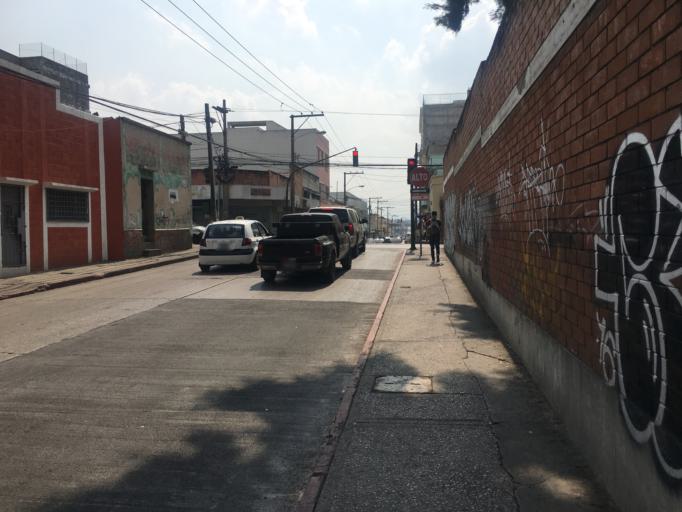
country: GT
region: Guatemala
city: Guatemala City
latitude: 14.6329
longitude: -90.5180
